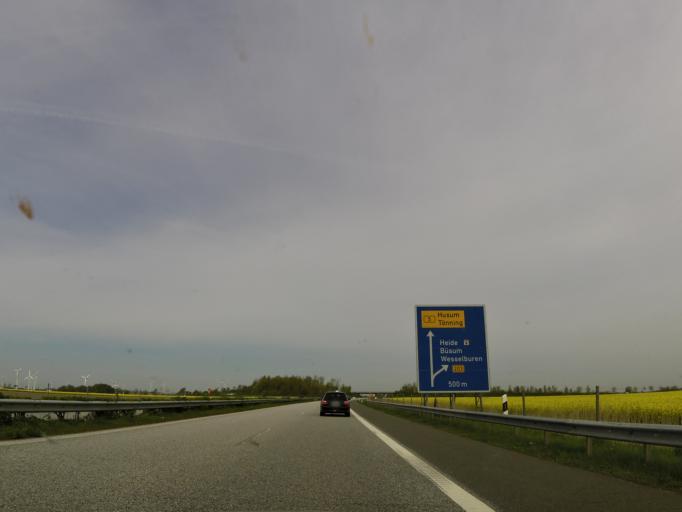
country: DE
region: Schleswig-Holstein
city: Lohe-Rickelshof
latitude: 54.1844
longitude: 9.0499
